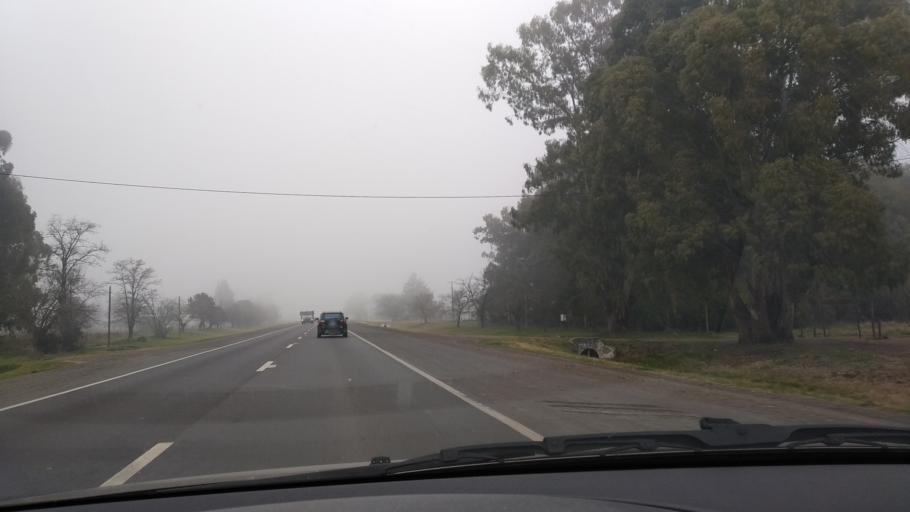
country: AR
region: Buenos Aires
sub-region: Partido de Azul
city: Azul
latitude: -36.8234
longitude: -59.8776
